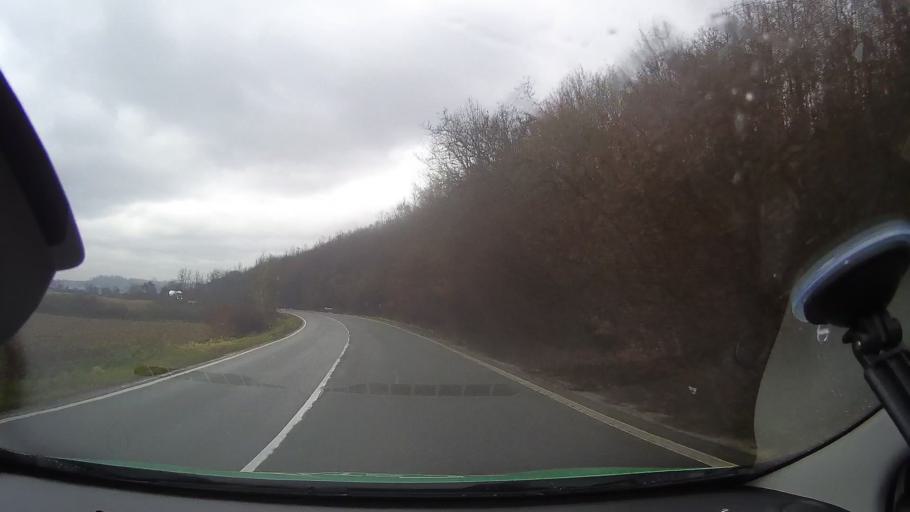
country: RO
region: Arad
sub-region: Comuna Almas
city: Almas
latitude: 46.2965
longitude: 22.2038
